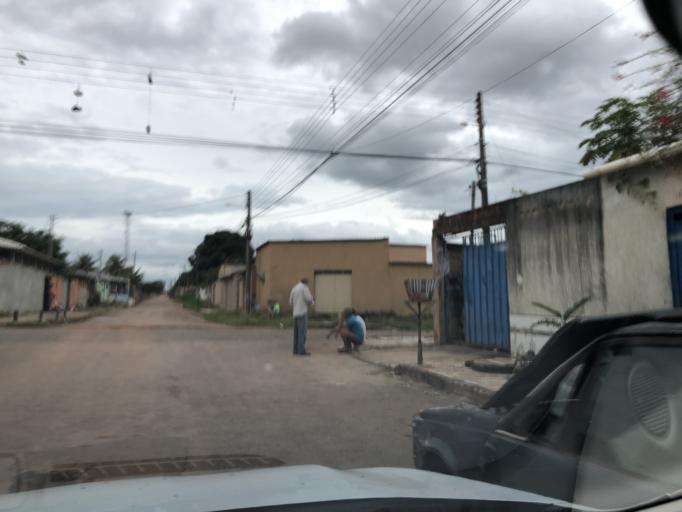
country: BR
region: Goias
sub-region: Luziania
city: Luziania
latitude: -16.1523
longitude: -47.9432
